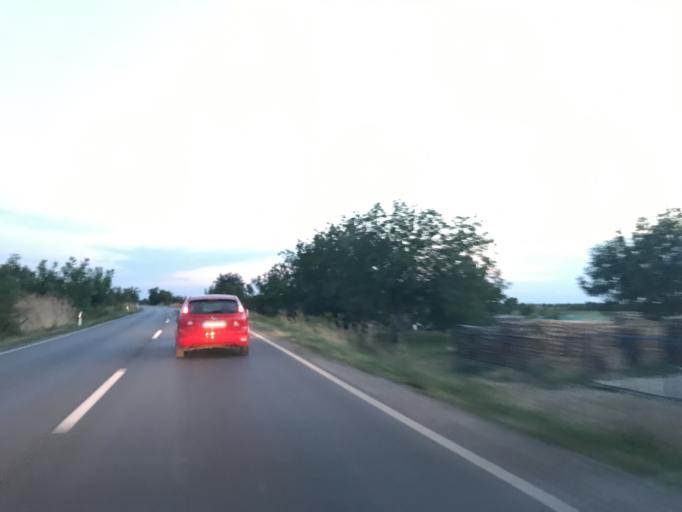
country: RS
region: Central Serbia
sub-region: Branicevski Okrug
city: Pozarevac
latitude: 44.6345
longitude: 21.1465
